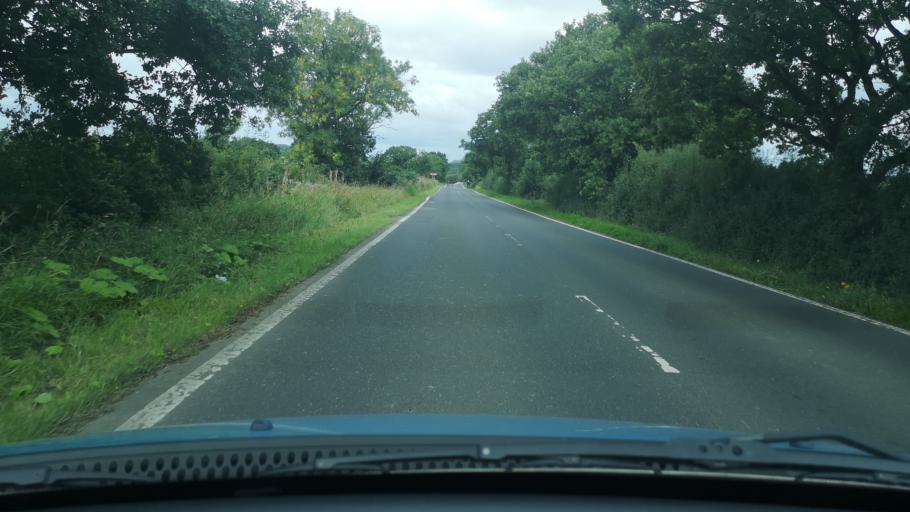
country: GB
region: England
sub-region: Barnsley
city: Royston
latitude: 53.6206
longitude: -1.4452
